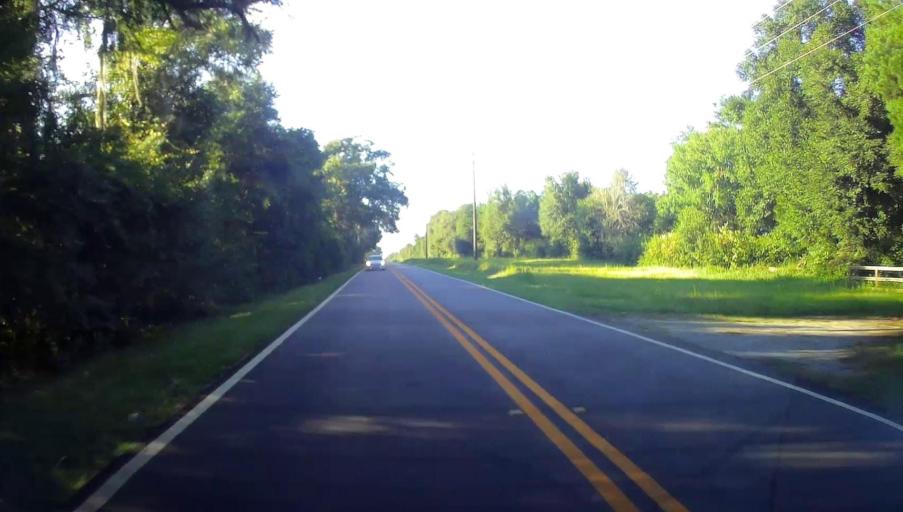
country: US
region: Georgia
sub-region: Pulaski County
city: Hawkinsville
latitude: 32.3051
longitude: -83.4506
